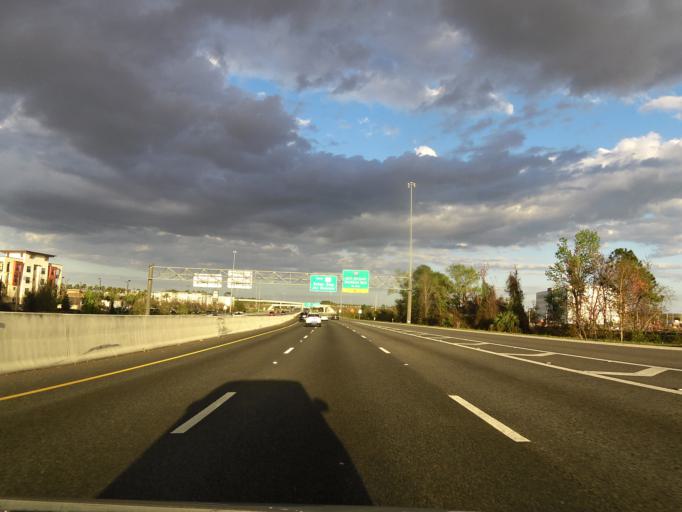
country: US
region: Florida
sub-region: Duval County
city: Jacksonville Beach
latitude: 30.2508
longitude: -81.5279
